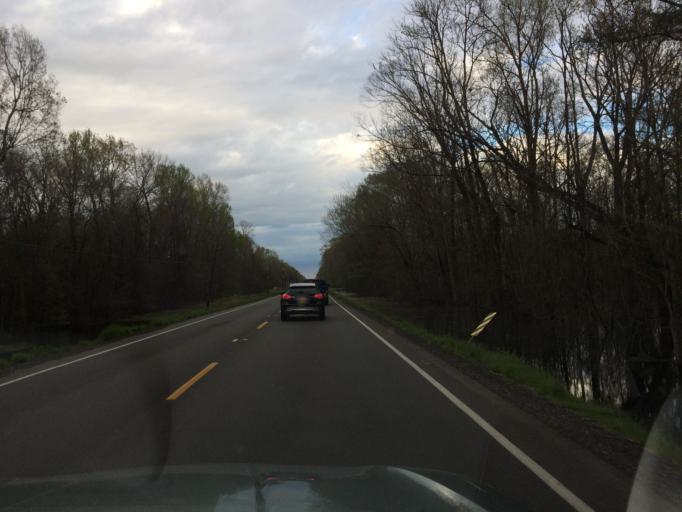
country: US
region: Louisiana
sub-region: West Baton Rouge Parish
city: Erwinville
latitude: 30.4609
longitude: -91.4195
